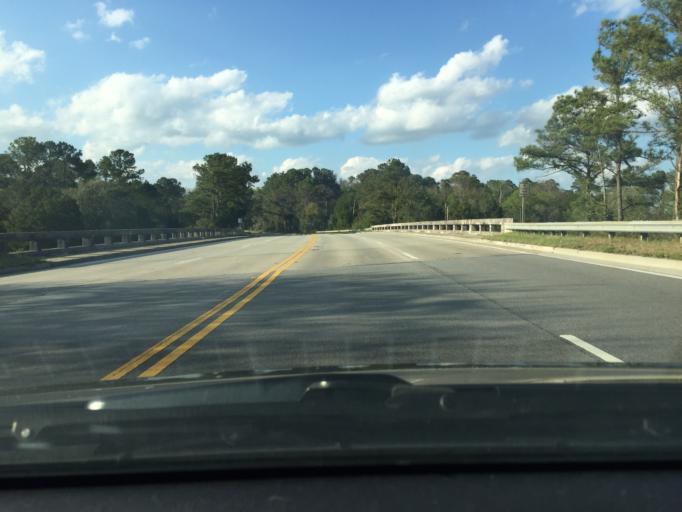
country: US
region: Georgia
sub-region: Chatham County
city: Isle of Hope
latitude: 31.9877
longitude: -81.1049
